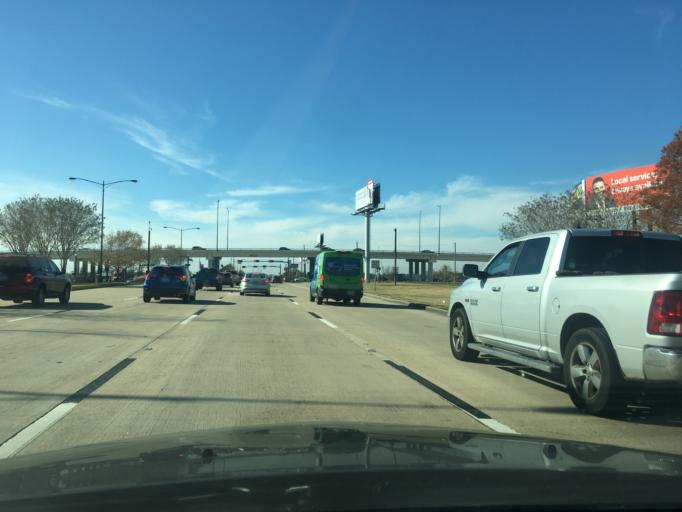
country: US
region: Texas
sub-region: Fort Bend County
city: Sugar Land
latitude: 29.6146
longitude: -95.6476
